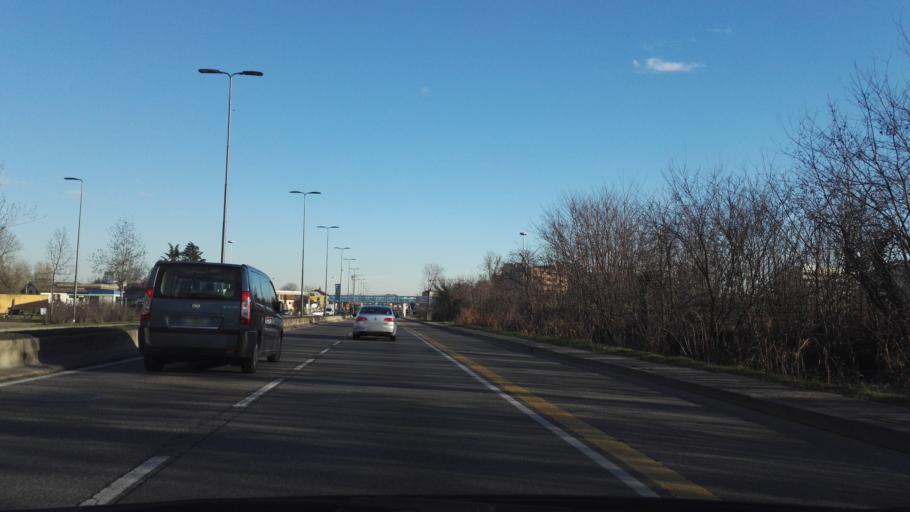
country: IT
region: Lombardy
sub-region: Citta metropolitana di Milano
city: Figino
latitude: 45.4807
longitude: 9.0987
